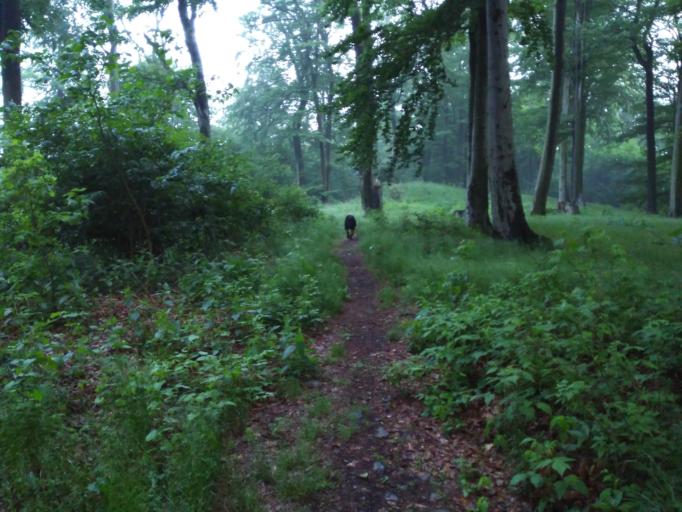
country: CZ
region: Central Bohemia
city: Hudlice
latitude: 49.9621
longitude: 13.9292
